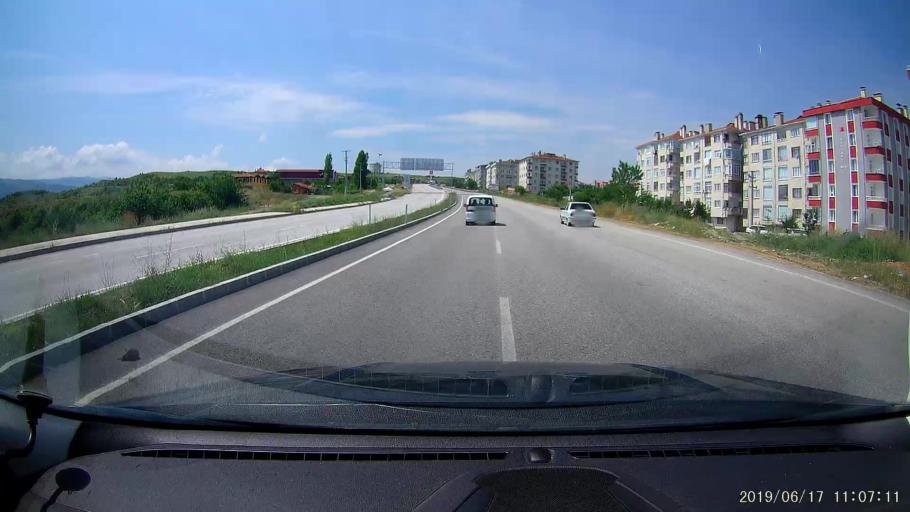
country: TR
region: Kastamonu
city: Tosya
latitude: 41.0059
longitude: 34.0570
